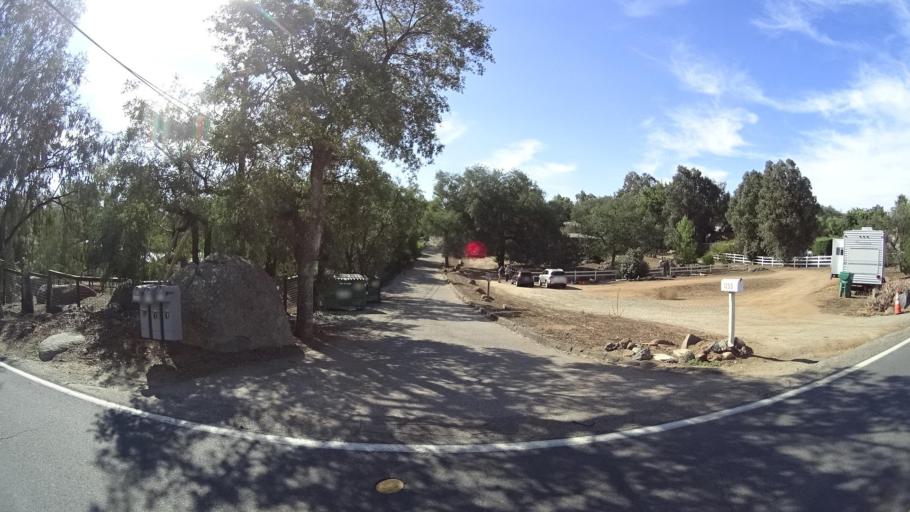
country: US
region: California
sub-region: San Diego County
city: Alpine
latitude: 32.8191
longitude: -116.7871
